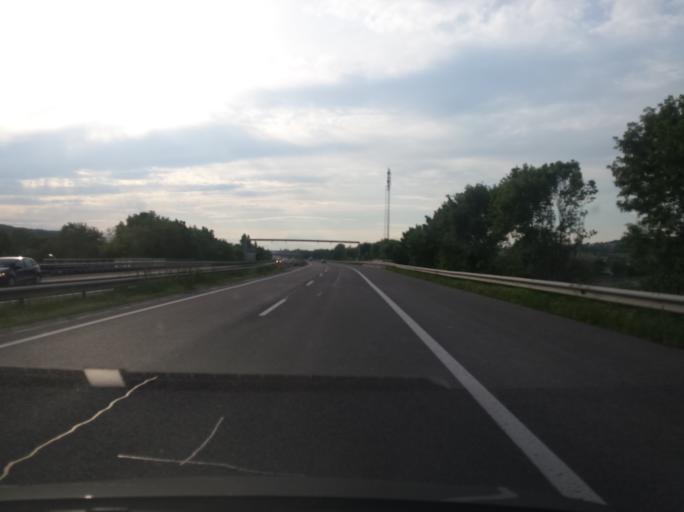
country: AT
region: Burgenland
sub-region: Eisenstadt-Umgebung
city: Mullendorf
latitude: 47.8241
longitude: 16.4832
